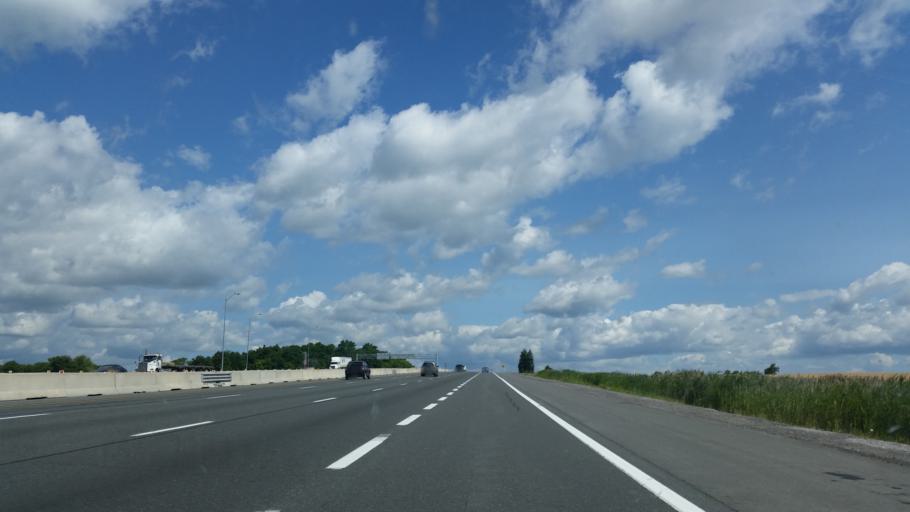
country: CA
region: Ontario
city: Vaughan
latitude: 43.9218
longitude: -79.5661
